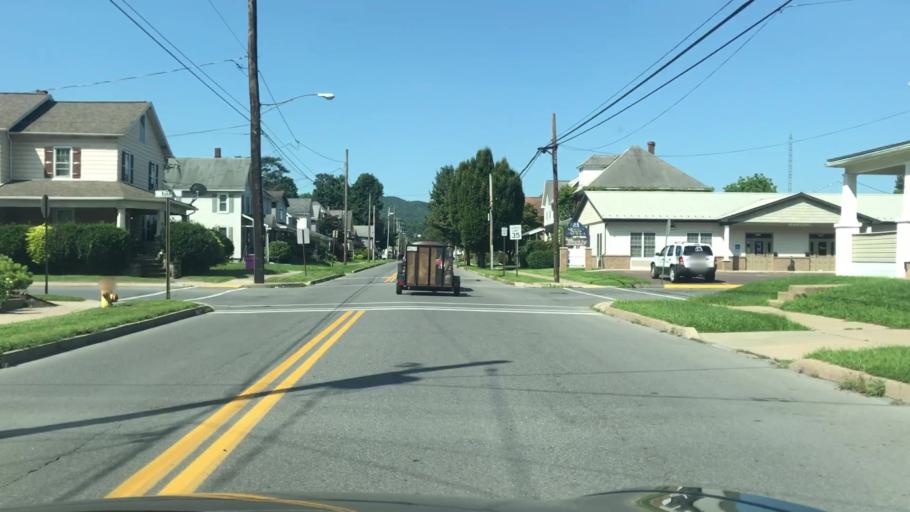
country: US
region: Pennsylvania
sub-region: Lycoming County
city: South Williamsport
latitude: 41.2301
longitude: -77.0041
